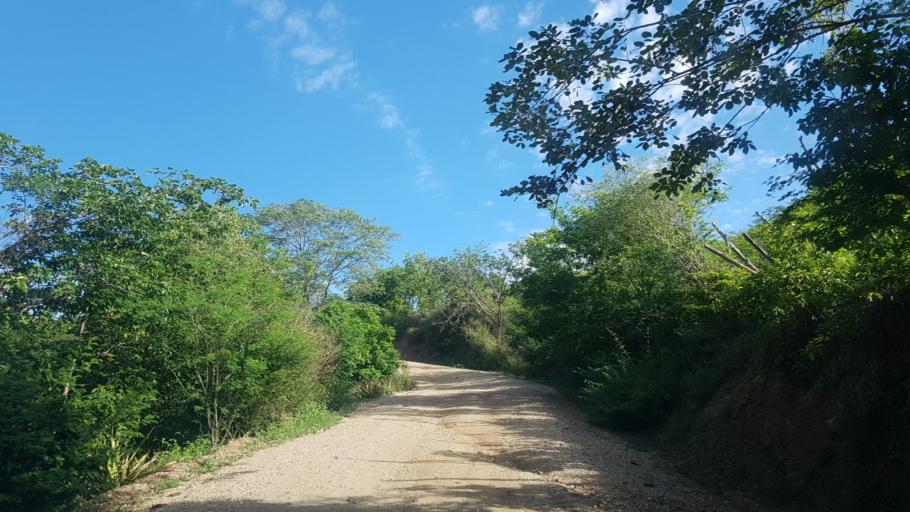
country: NI
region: Nueva Segovia
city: Ocotal
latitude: 13.6083
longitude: -86.4607
